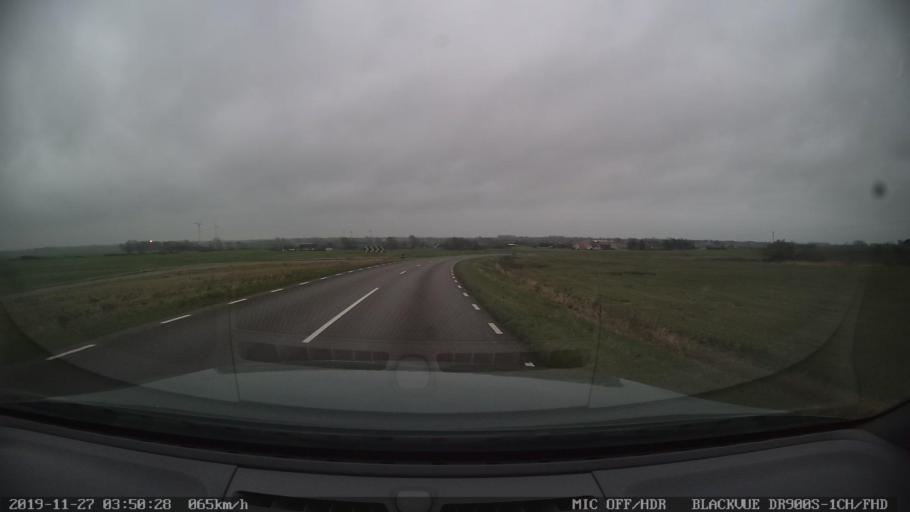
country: SE
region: Skane
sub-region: Hoganas Kommun
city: Hoganas
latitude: 56.2521
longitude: 12.5691
